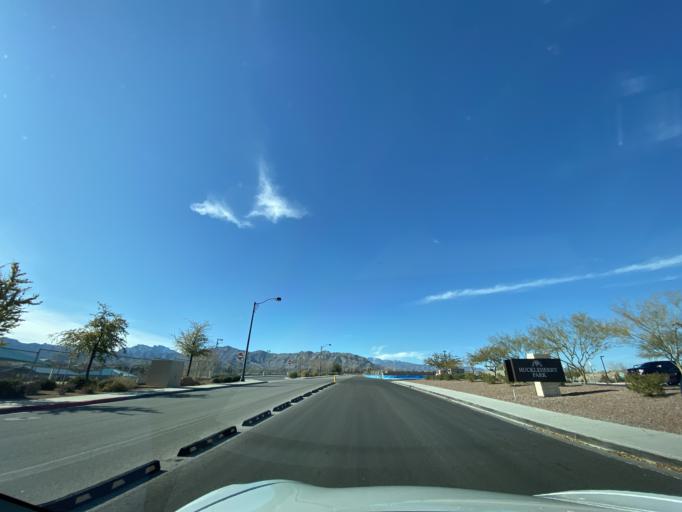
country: US
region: Nevada
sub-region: Clark County
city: Summerlin South
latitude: 36.2975
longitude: -115.3206
